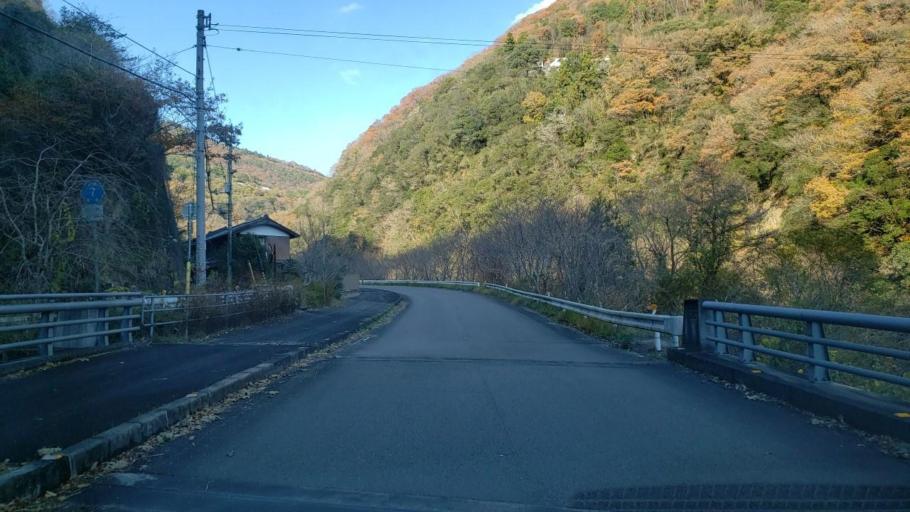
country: JP
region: Tokushima
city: Wakimachi
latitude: 34.0920
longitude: 134.0682
